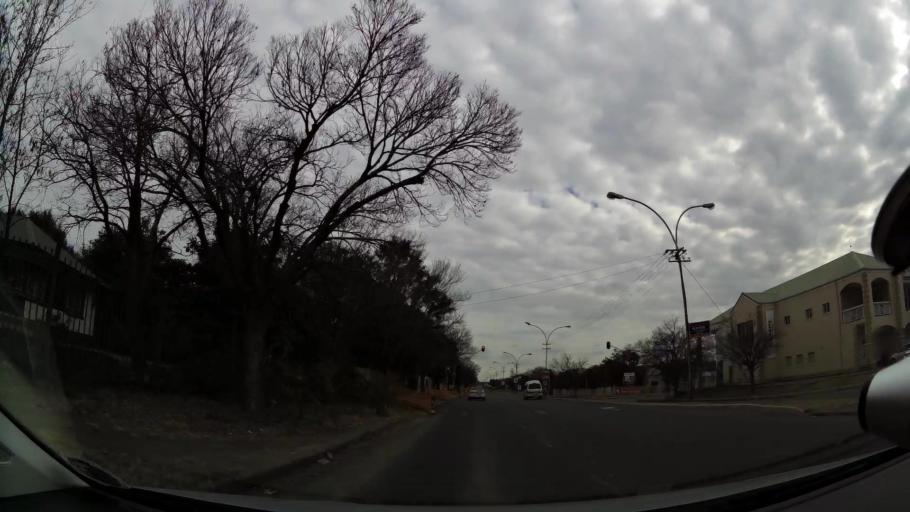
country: ZA
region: Orange Free State
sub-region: Mangaung Metropolitan Municipality
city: Bloemfontein
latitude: -29.0892
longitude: 26.2129
